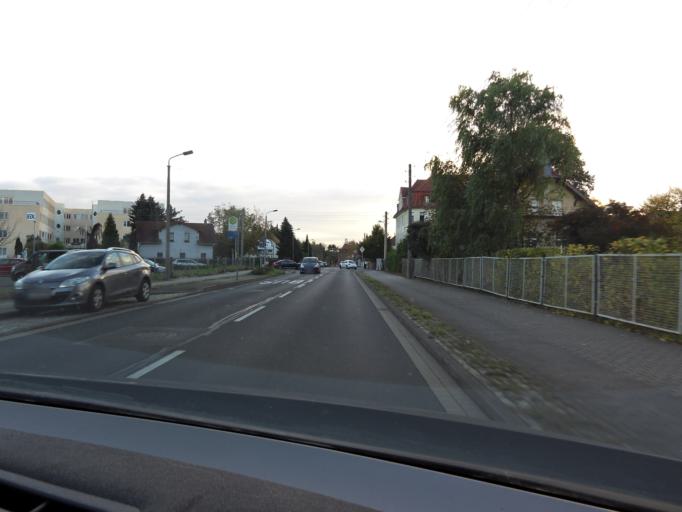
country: DE
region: Saxony
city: Leipzig
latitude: 51.3847
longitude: 12.3241
